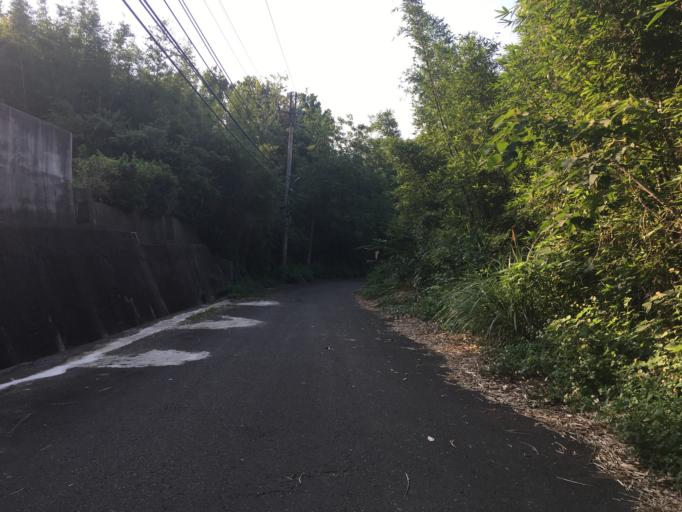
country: TW
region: Taiwan
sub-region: Hsinchu
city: Hsinchu
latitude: 24.7385
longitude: 120.9880
